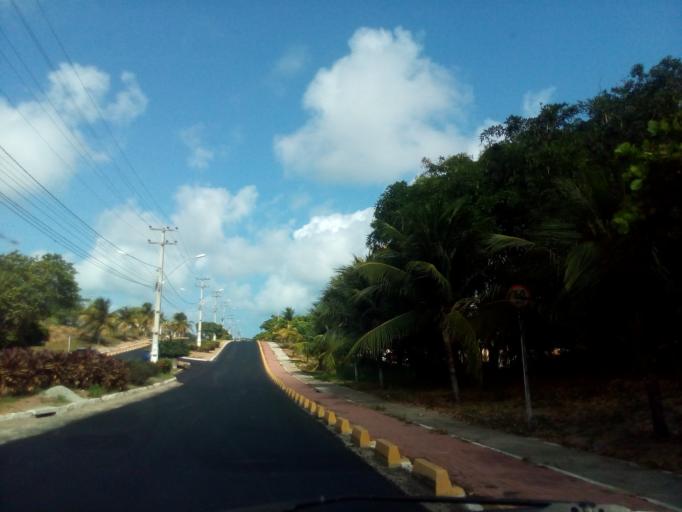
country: BR
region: Rio Grande do Norte
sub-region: Natal
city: Natal
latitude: -5.8383
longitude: -35.2091
